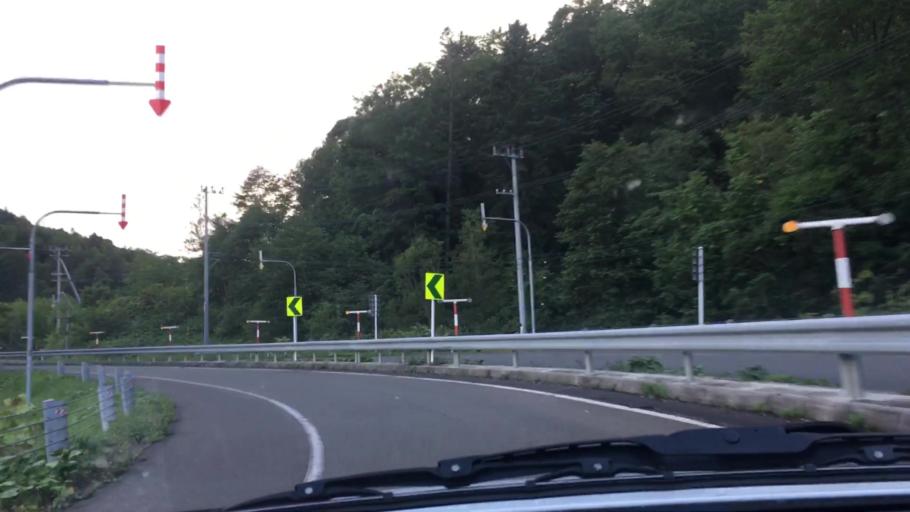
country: JP
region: Hokkaido
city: Shimo-furano
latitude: 43.0470
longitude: 142.4723
